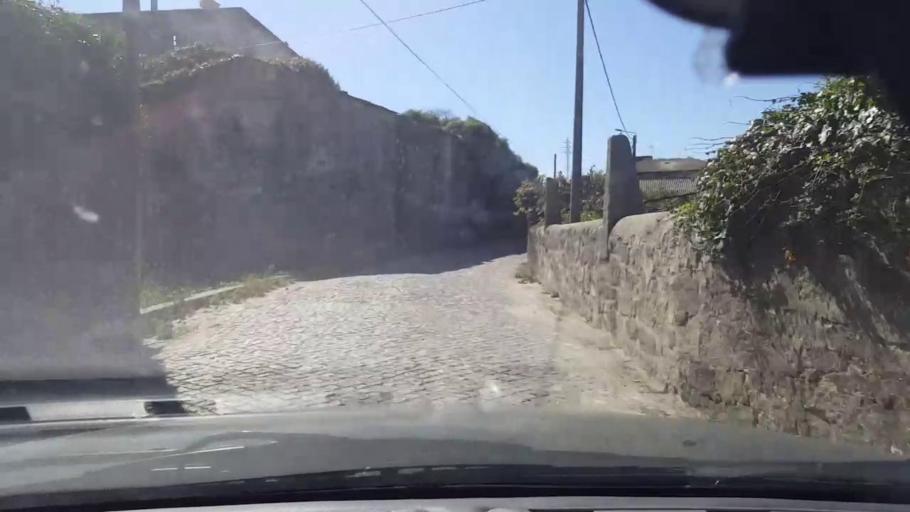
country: PT
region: Porto
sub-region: Maia
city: Gemunde
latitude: 41.2923
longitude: -8.6490
